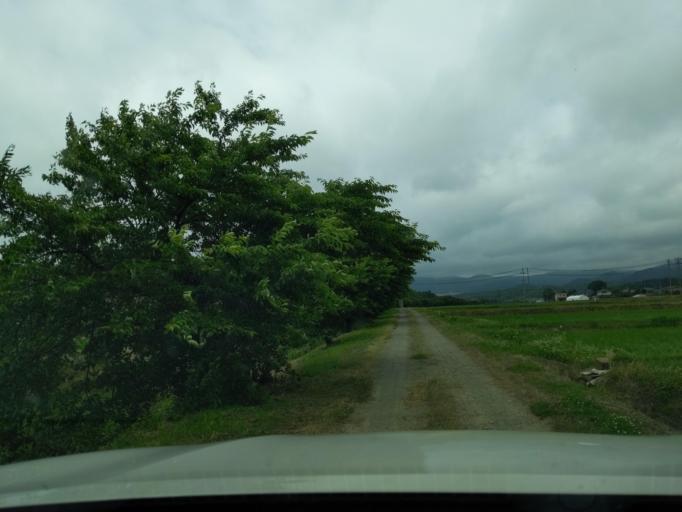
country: JP
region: Fukushima
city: Koriyama
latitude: 37.4519
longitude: 140.3231
